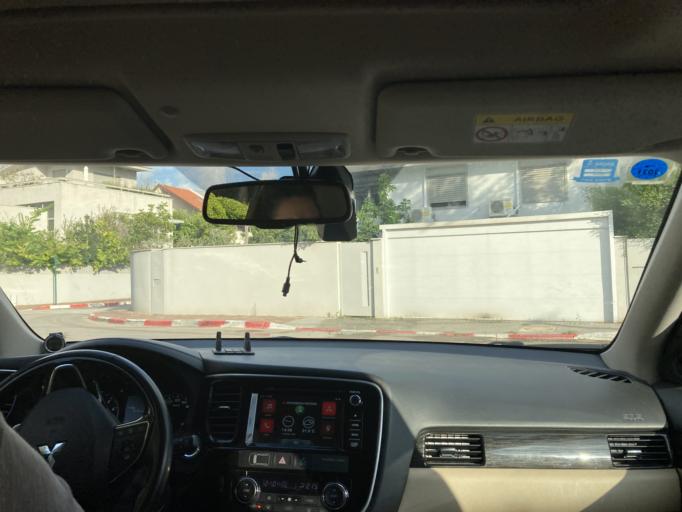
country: IL
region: Tel Aviv
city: Ramat HaSharon
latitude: 32.1519
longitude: 34.8359
